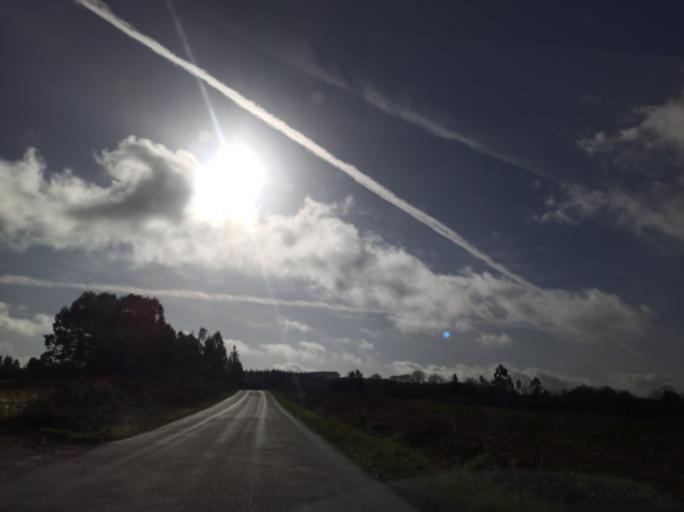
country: ES
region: Galicia
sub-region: Provincia da Coruna
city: Sobrado
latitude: 43.0872
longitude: -7.9668
